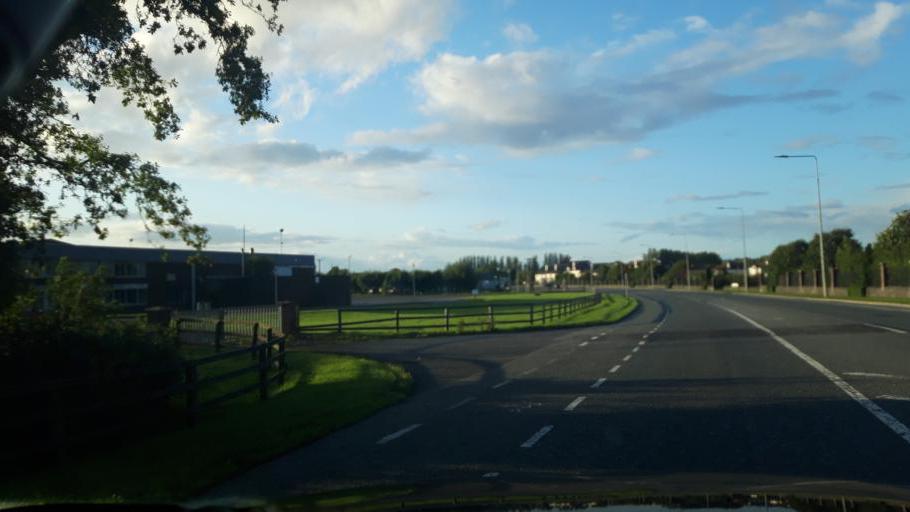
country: IE
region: Leinster
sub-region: An Iarmhi
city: Athlone
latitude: 53.4327
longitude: -7.9014
